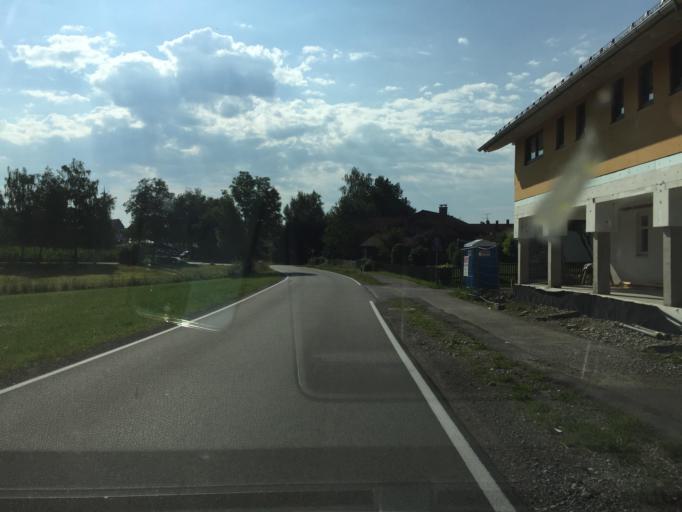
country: DE
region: Bavaria
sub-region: Upper Bavaria
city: Tuntenhausen
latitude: 47.9511
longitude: 12.0274
